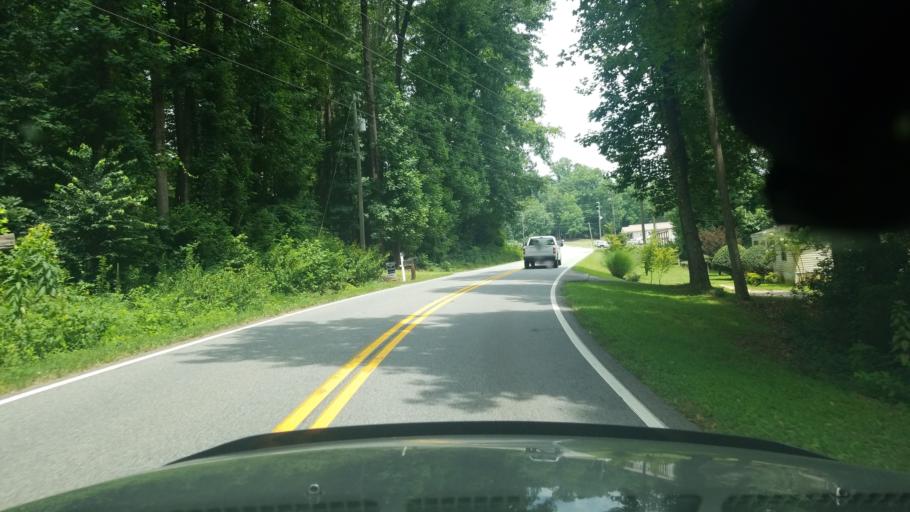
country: US
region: Georgia
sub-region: Forsyth County
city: Cumming
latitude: 34.2127
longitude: -84.2064
